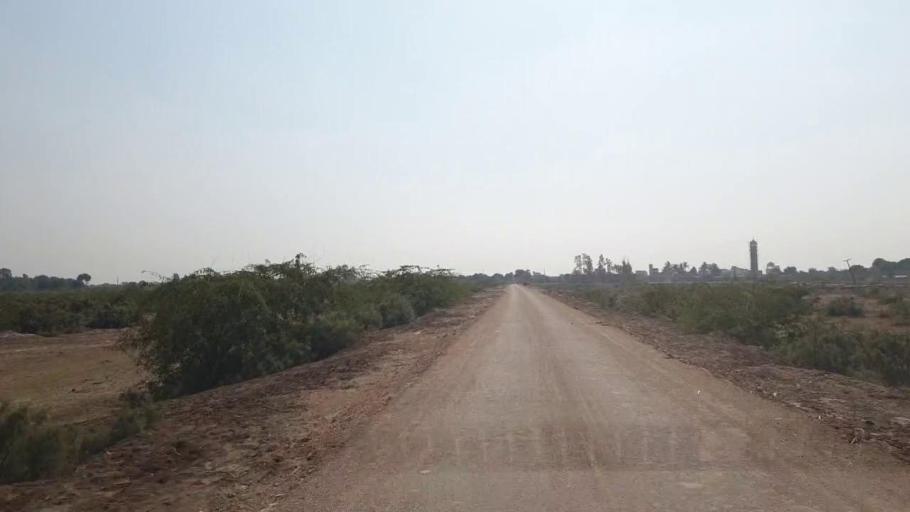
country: PK
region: Sindh
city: Chambar
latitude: 25.3793
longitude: 68.8808
